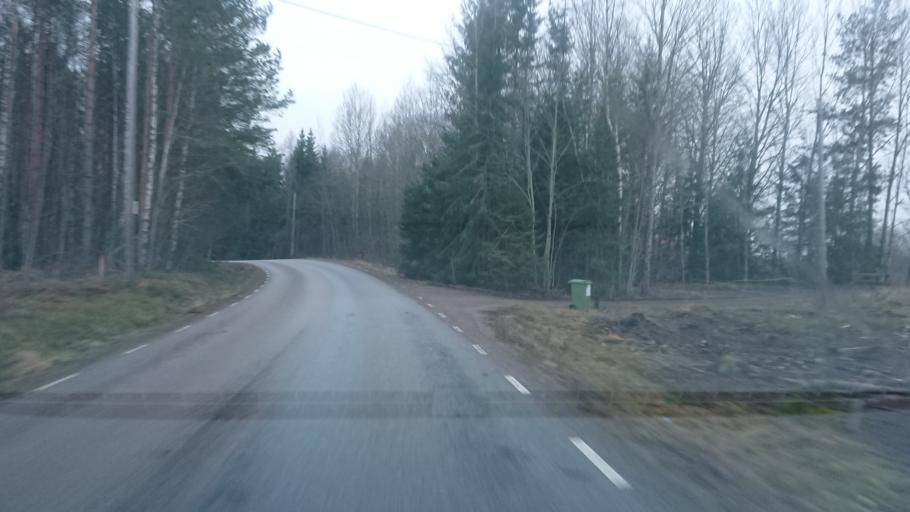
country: SE
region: Uppsala
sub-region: Osthammars Kommun
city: Bjorklinge
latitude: 60.0212
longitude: 17.5748
